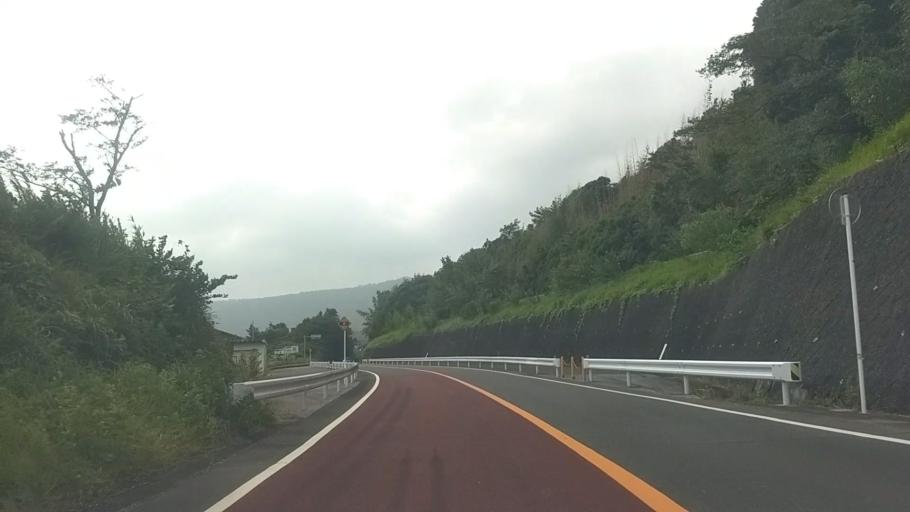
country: JP
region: Chiba
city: Kimitsu
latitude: 35.2477
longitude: 140.0053
